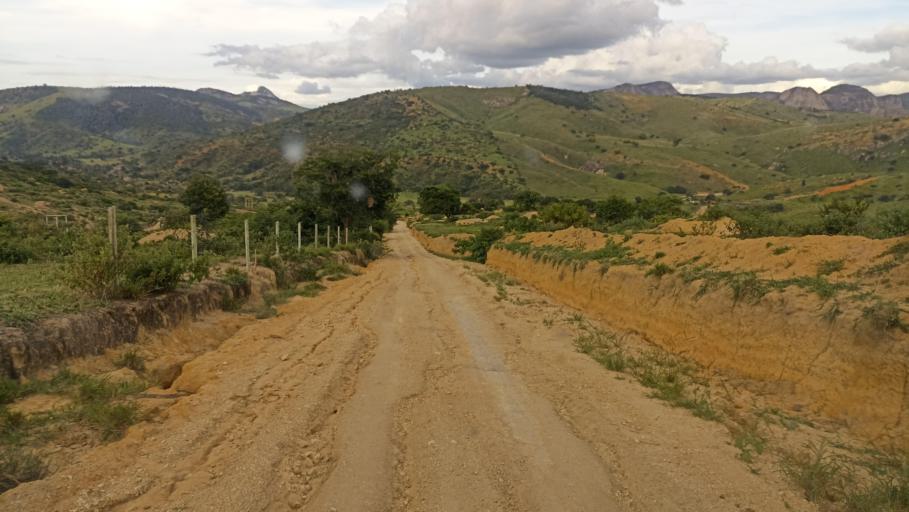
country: BR
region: Minas Gerais
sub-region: Almenara
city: Almenara
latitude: -16.5430
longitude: -40.4473
